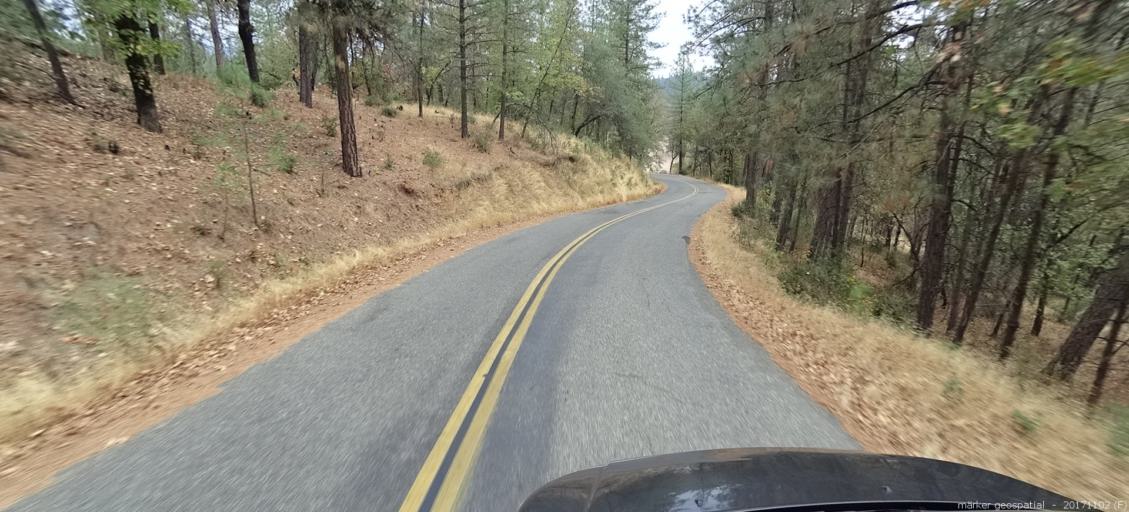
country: US
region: California
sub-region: Shasta County
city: Bella Vista
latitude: 40.7387
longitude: -122.2391
